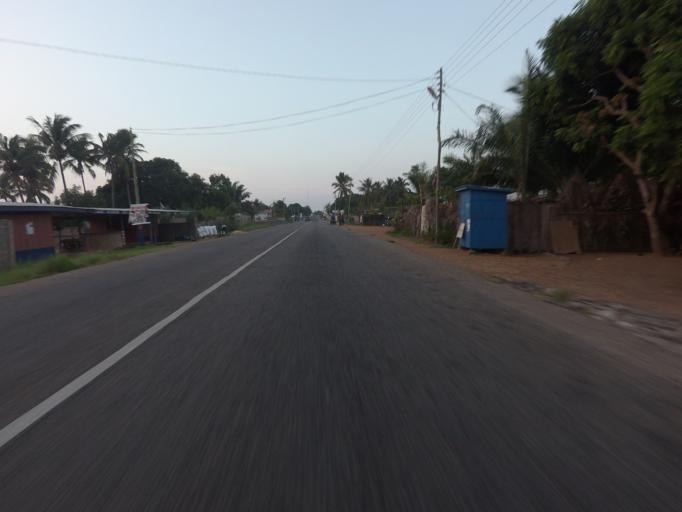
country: GH
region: Volta
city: Keta
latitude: 5.8723
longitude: 0.9798
